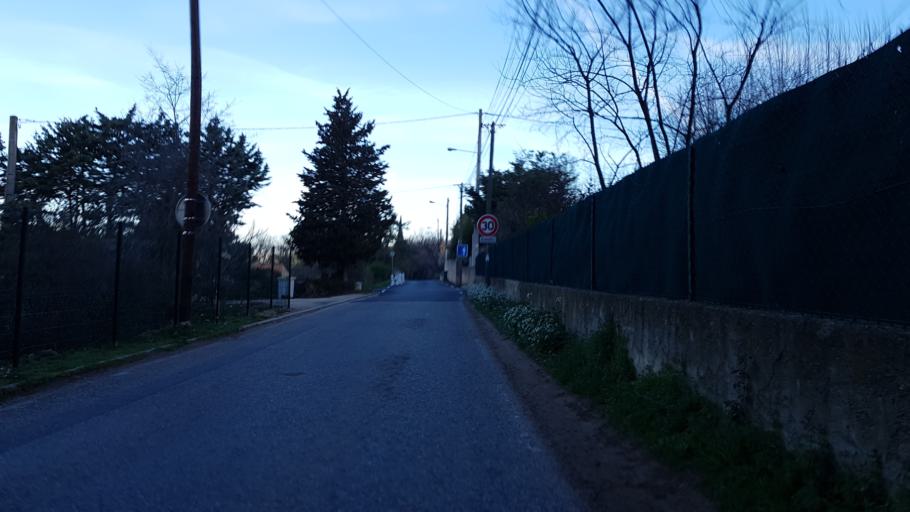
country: FR
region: Provence-Alpes-Cote d'Azur
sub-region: Departement des Bouches-du-Rhone
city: Bouc-Bel-Air
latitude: 43.4922
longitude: 5.4128
